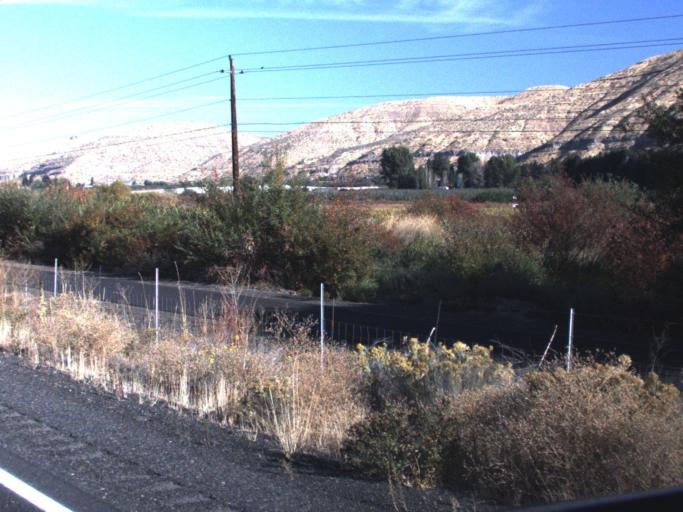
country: US
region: Washington
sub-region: Yakima County
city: Gleed
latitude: 46.7030
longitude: -120.6595
